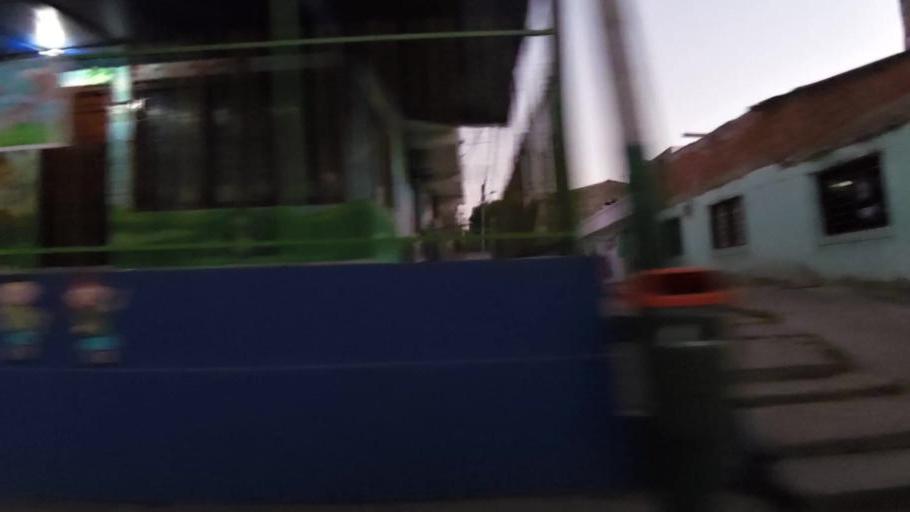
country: CO
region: Bolivar
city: Cartagena
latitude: 10.3876
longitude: -75.4946
